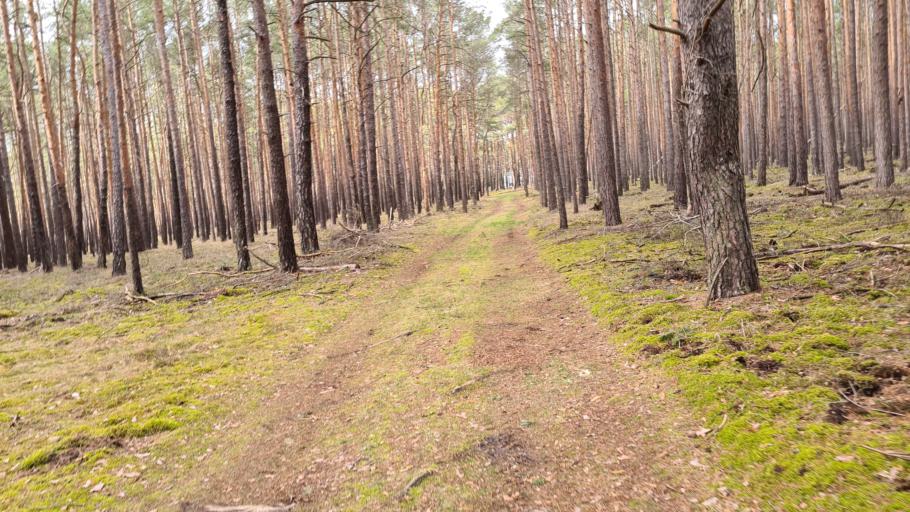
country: DE
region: Brandenburg
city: Schilda
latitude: 51.6121
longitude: 13.4000
